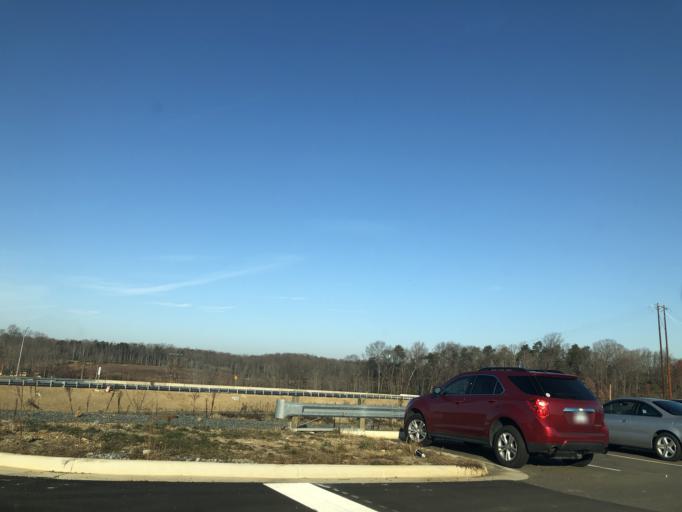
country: US
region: Virginia
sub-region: Stafford County
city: Stafford
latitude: 38.4204
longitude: -77.4196
